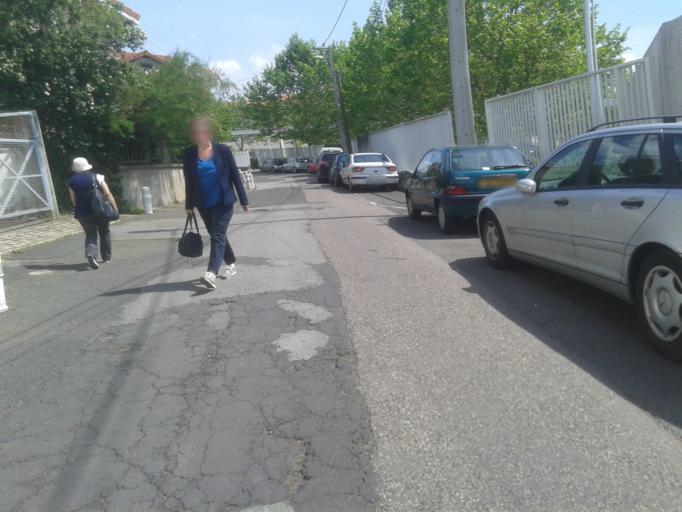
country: FR
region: Auvergne
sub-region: Departement du Puy-de-Dome
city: Clermont-Ferrand
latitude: 45.7843
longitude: 3.0887
